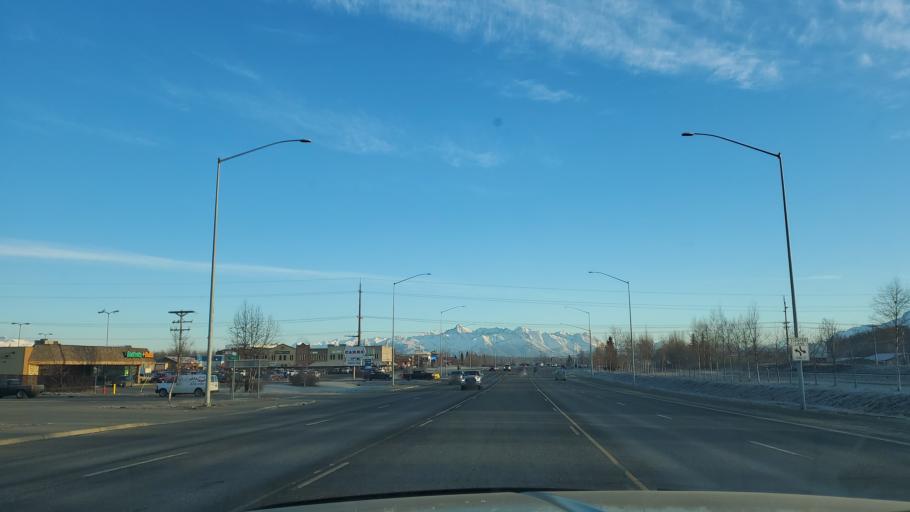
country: US
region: Alaska
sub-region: Matanuska-Susitna Borough
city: Wasilla
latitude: 61.5809
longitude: -149.4385
